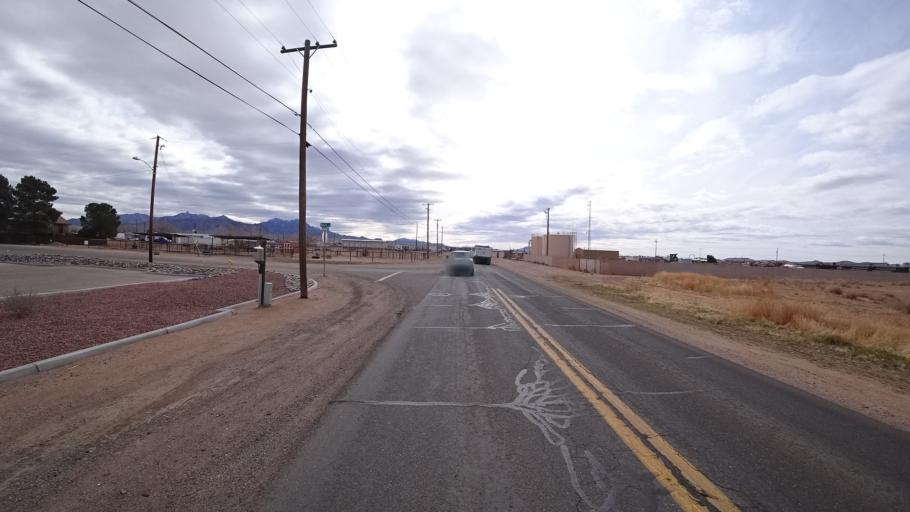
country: US
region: Arizona
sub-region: Mohave County
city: New Kingman-Butler
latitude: 35.2407
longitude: -113.9938
